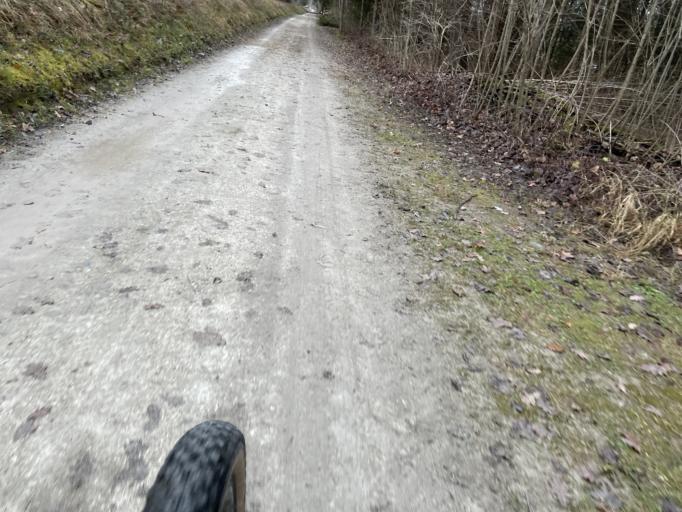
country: CH
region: Bern
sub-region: Bern-Mittelland District
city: Munsingen
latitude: 46.8558
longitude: 7.5552
